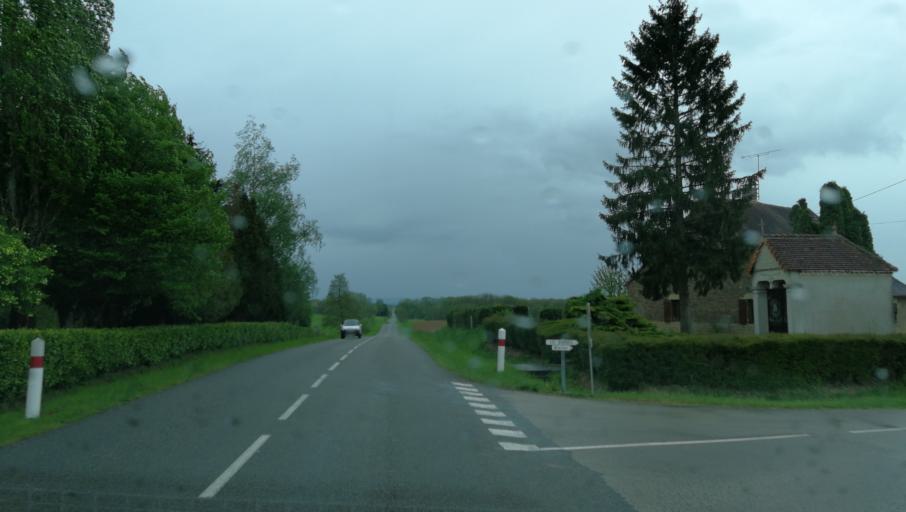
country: FR
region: Franche-Comte
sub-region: Departement du Jura
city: Bletterans
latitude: 46.8029
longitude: 5.4002
